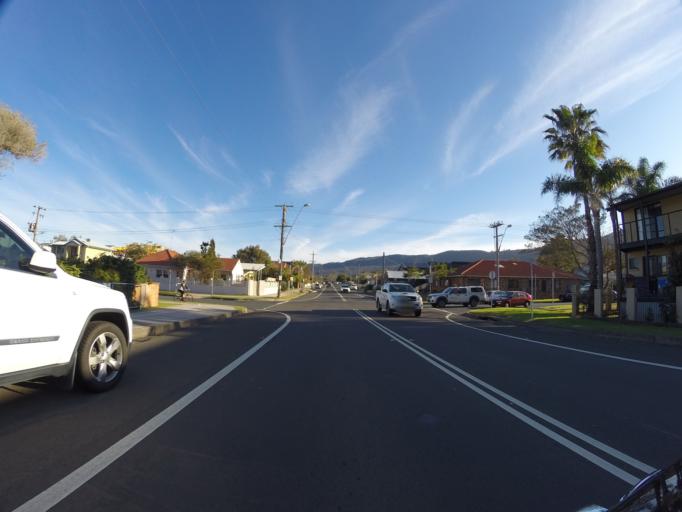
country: AU
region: New South Wales
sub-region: Wollongong
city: Bulli
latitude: -34.3123
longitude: 150.9289
